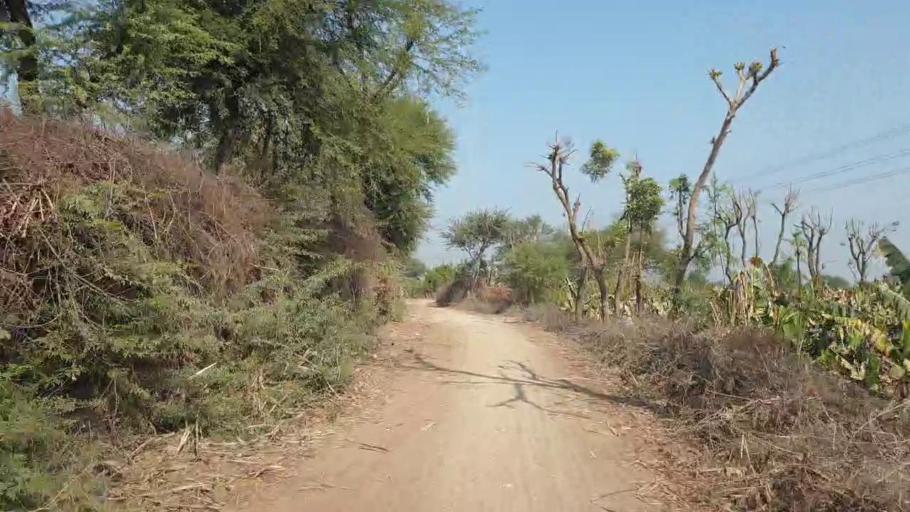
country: PK
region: Sindh
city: Bhit Shah
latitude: 25.7254
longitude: 68.5401
